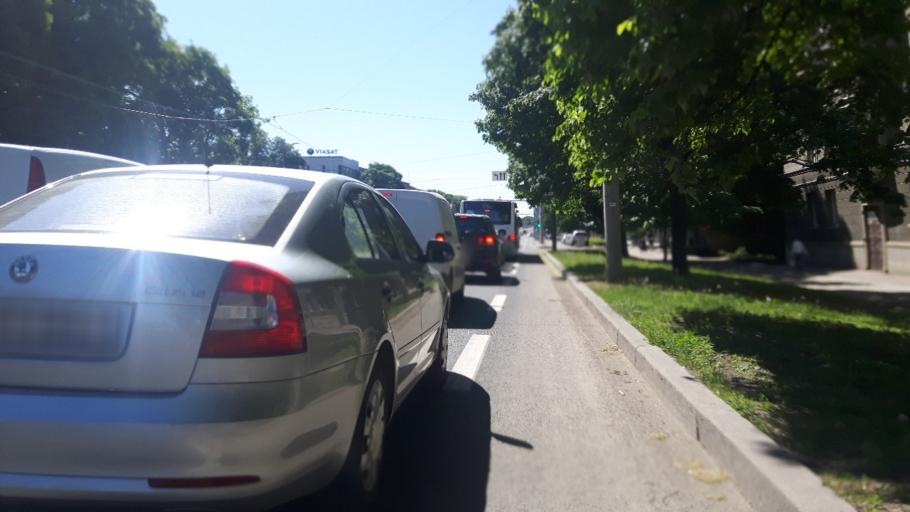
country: EE
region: Harju
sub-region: Tallinna linn
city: Tallinn
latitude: 59.4260
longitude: 24.7424
